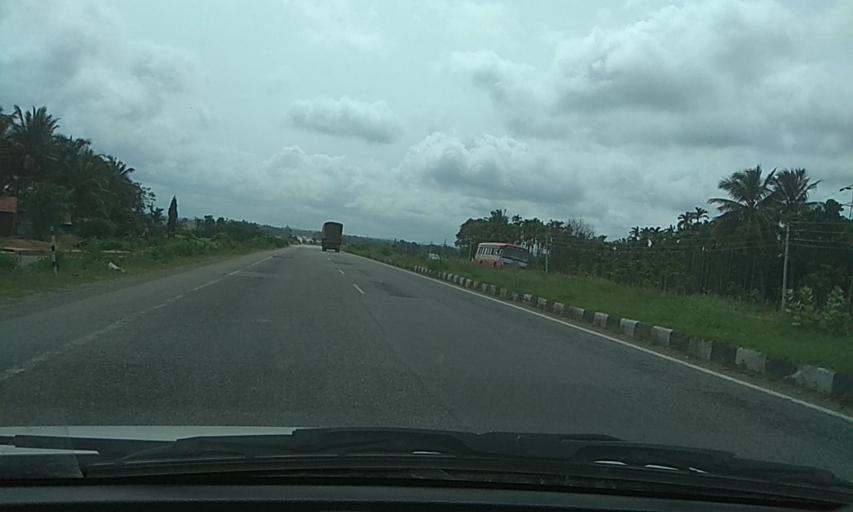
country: IN
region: Karnataka
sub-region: Davanagere
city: Mayakonda
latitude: 14.4057
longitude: 75.9986
